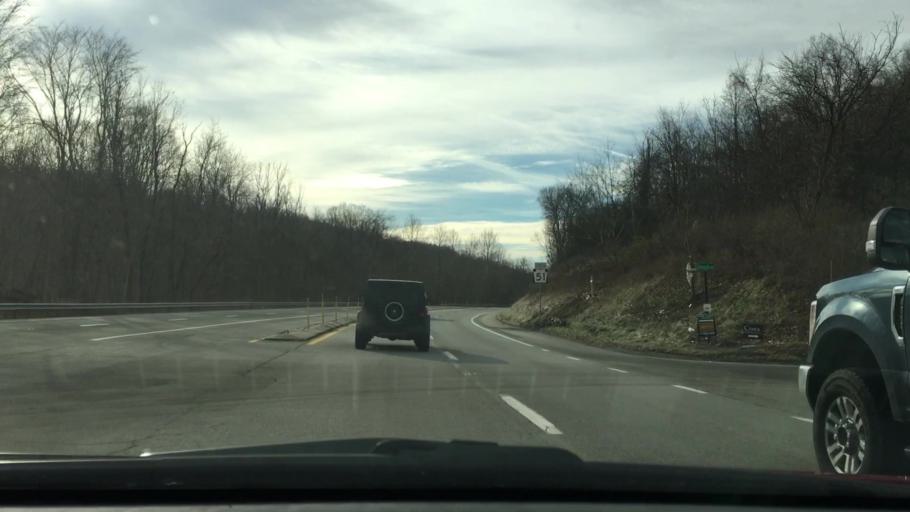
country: US
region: Pennsylvania
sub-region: Fayette County
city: Perryopolis
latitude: 40.0015
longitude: -79.7616
